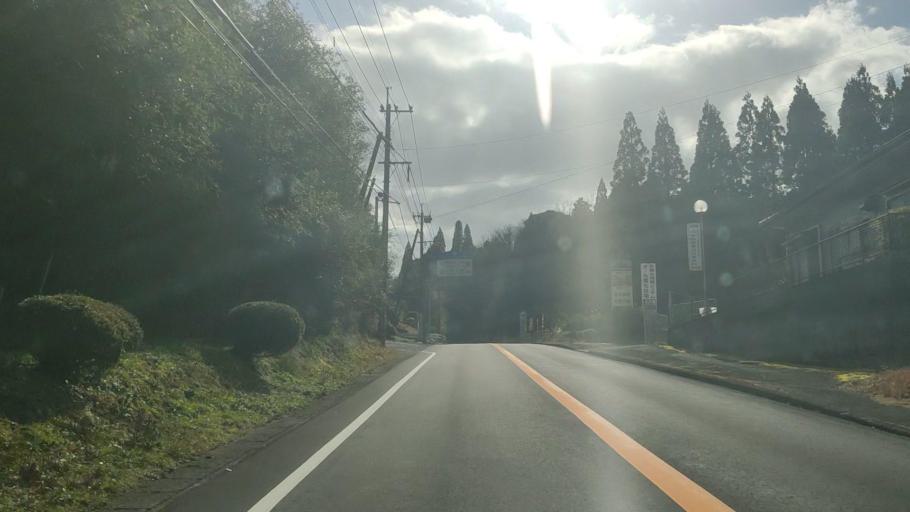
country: JP
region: Kagoshima
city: Kajiki
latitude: 31.8286
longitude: 130.6889
